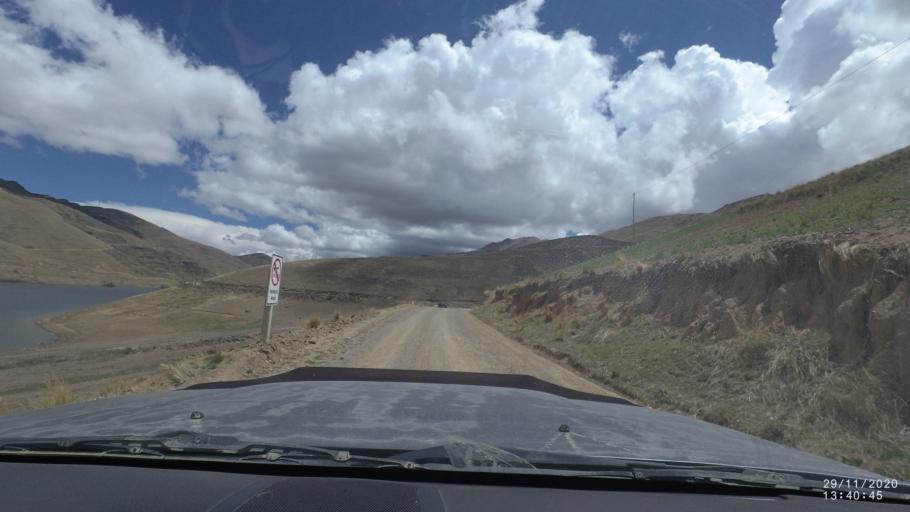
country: BO
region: Cochabamba
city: Cochabamba
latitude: -17.1298
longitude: -66.3261
